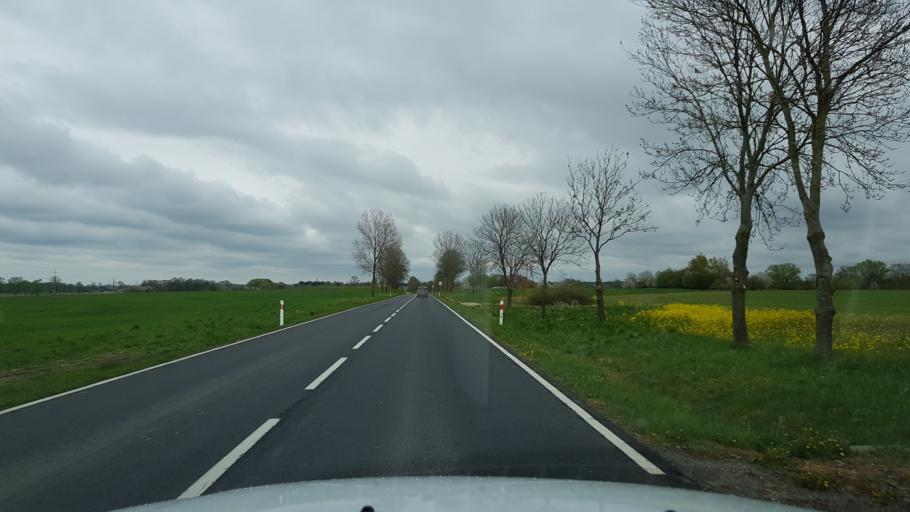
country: PL
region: West Pomeranian Voivodeship
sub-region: Powiat koszalinski
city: Mielno
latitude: 54.2088
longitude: 15.9715
